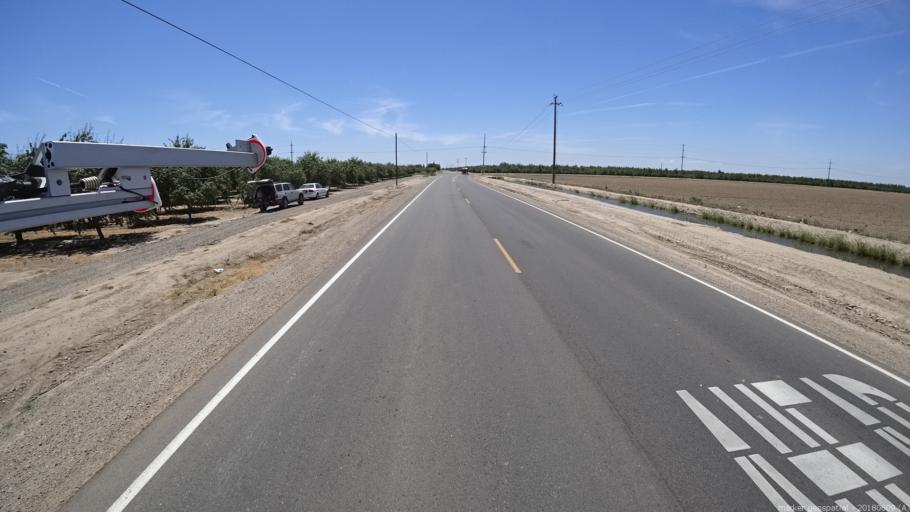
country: US
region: California
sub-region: Madera County
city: Parkwood
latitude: 36.9250
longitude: -120.0742
